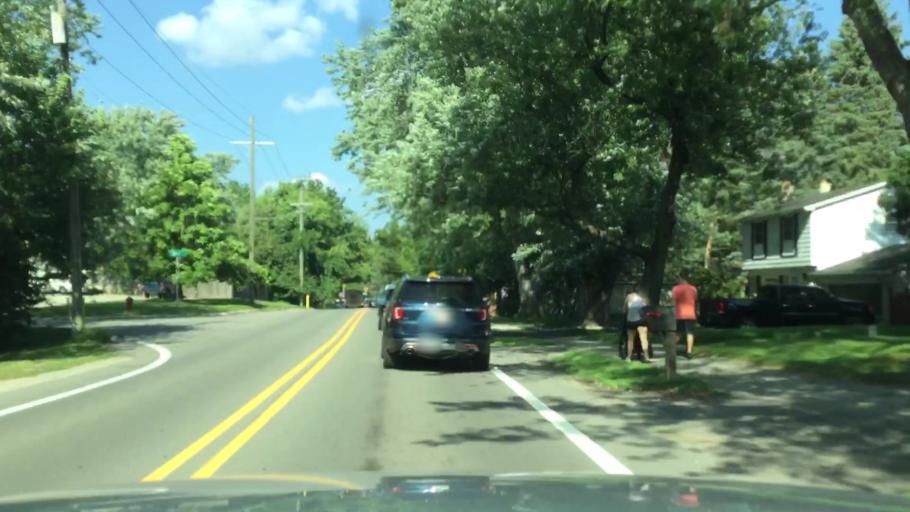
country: US
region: Michigan
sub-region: Oakland County
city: West Bloomfield Township
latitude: 42.5765
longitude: -83.4142
